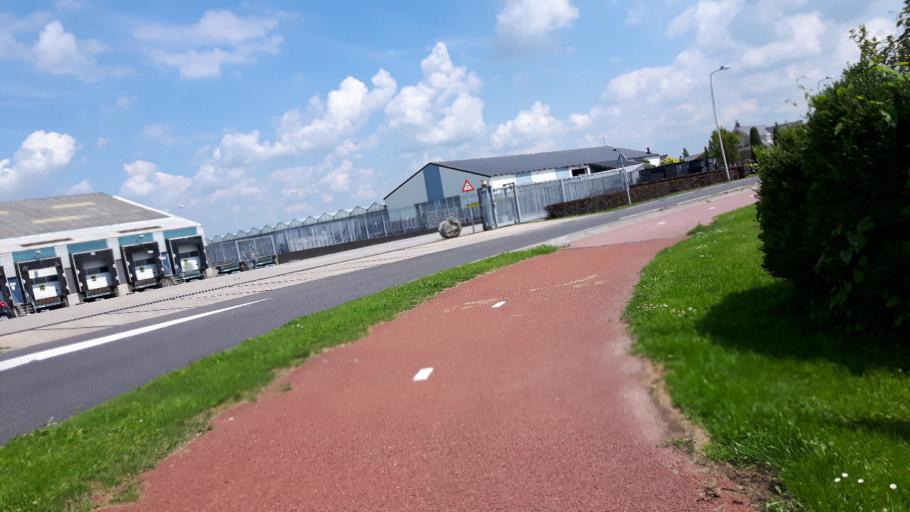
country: NL
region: South Holland
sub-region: Gemeente Boskoop
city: Boskoop
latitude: 52.0925
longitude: 4.6843
